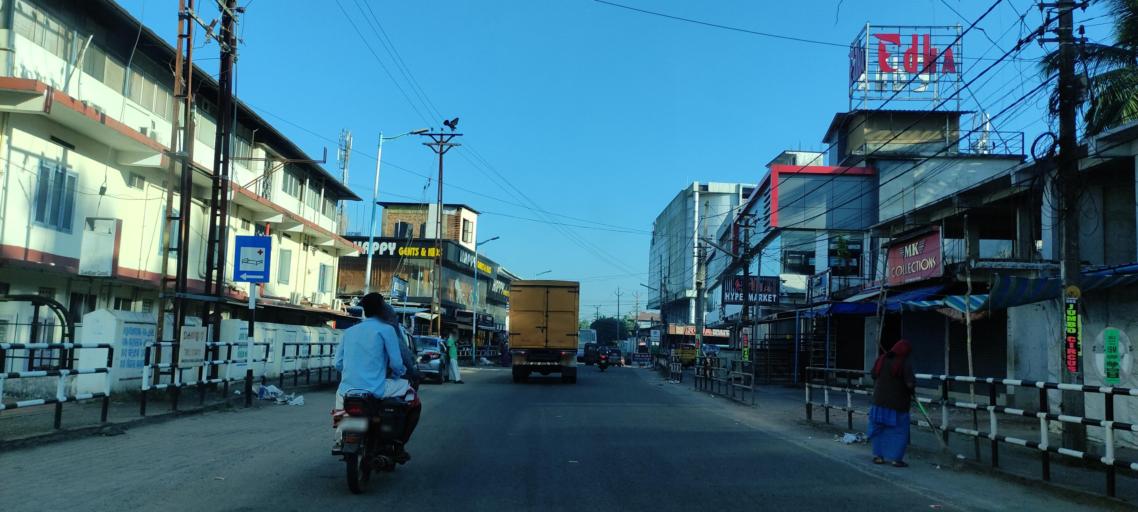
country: IN
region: Kerala
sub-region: Alappuzha
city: Kayankulam
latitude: 9.1729
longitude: 76.5000
